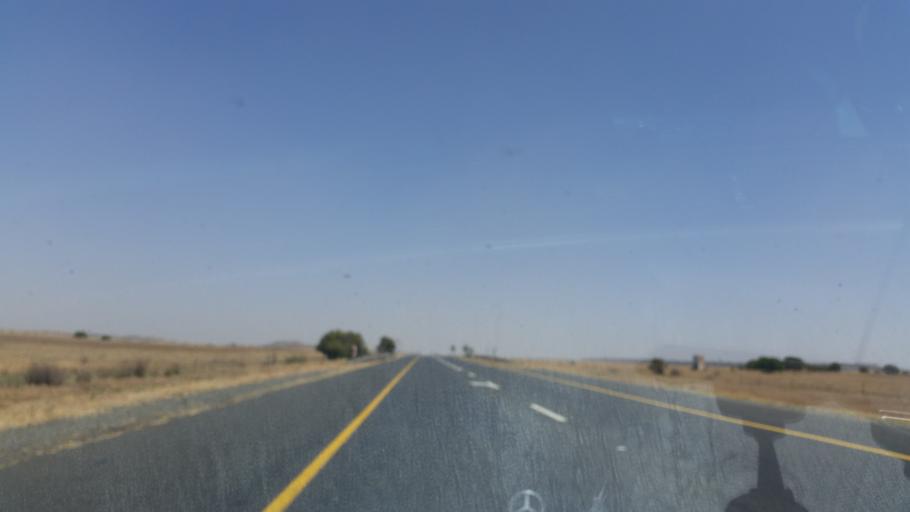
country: ZA
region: Orange Free State
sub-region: Lejweleputswa District Municipality
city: Winburg
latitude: -28.6790
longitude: 26.8323
